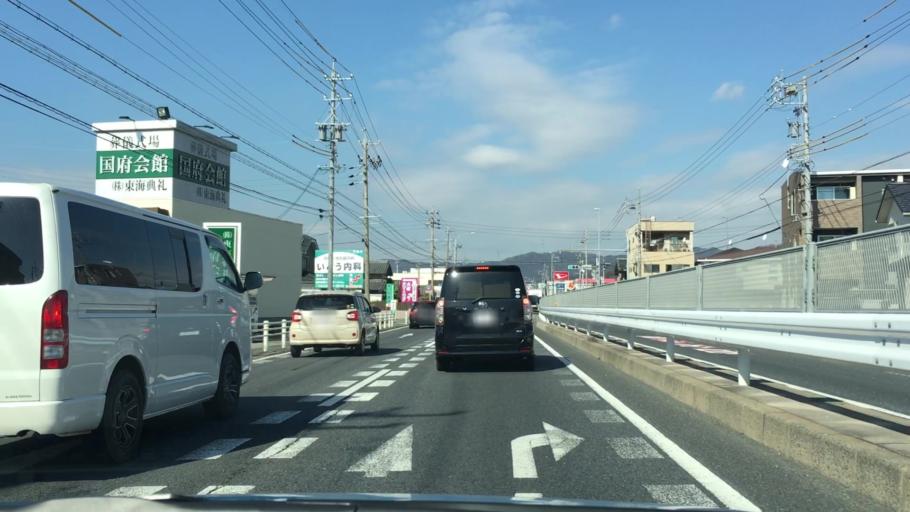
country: JP
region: Aichi
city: Kozakai-cho
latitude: 34.8336
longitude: 137.3291
